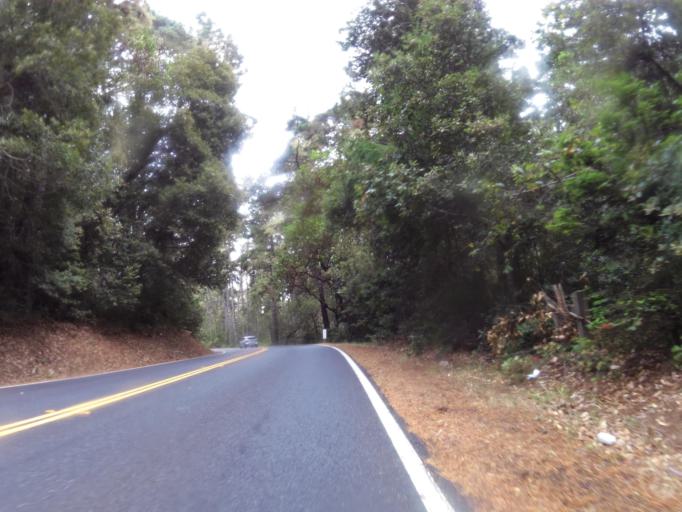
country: US
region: California
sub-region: Sonoma County
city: Sea Ranch
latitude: 38.5612
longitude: -123.3120
